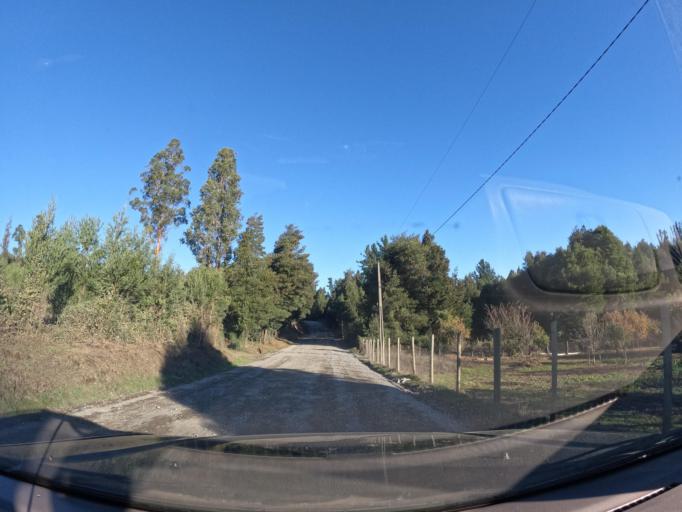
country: CL
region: Biobio
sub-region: Provincia de Concepcion
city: Chiguayante
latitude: -37.0181
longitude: -72.8920
